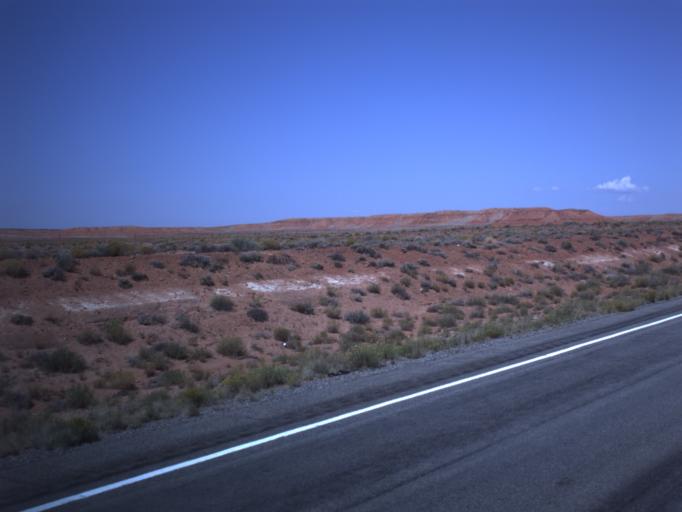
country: US
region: Utah
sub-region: San Juan County
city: Blanding
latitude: 36.9997
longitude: -109.6094
